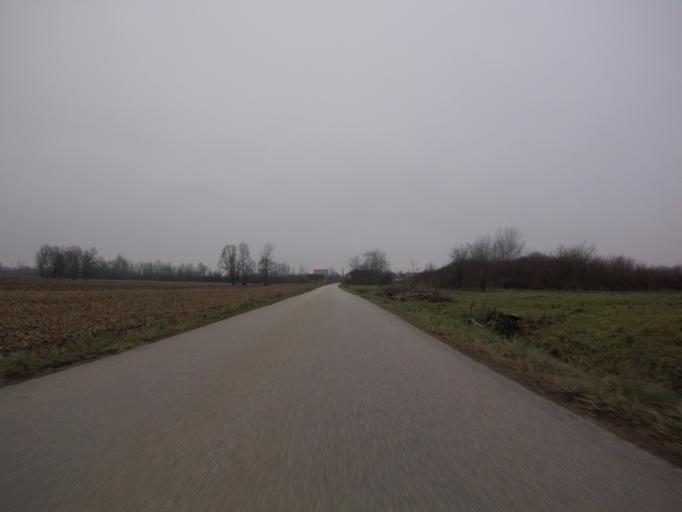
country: HR
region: Sisacko-Moslavacka
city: Lekenik
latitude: 45.6335
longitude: 16.2952
